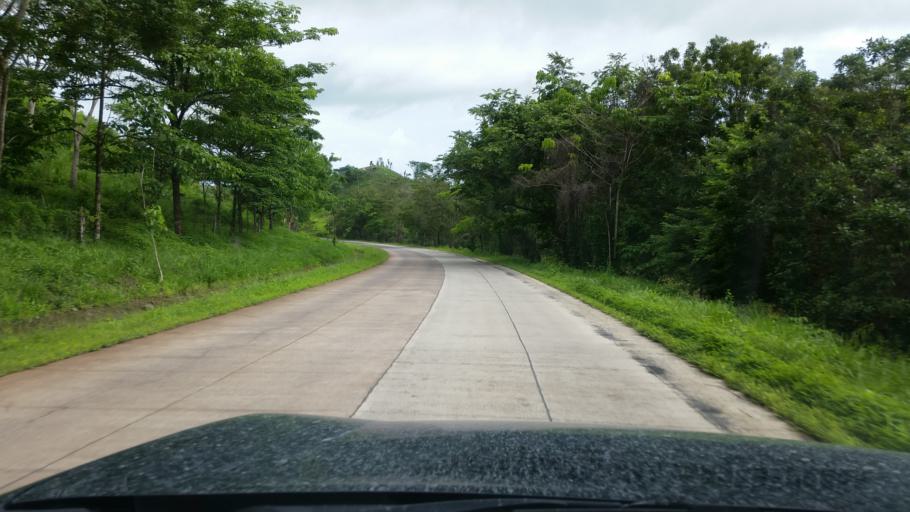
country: NI
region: Atlantico Norte (RAAN)
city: Siuna
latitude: 13.5396
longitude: -84.8243
